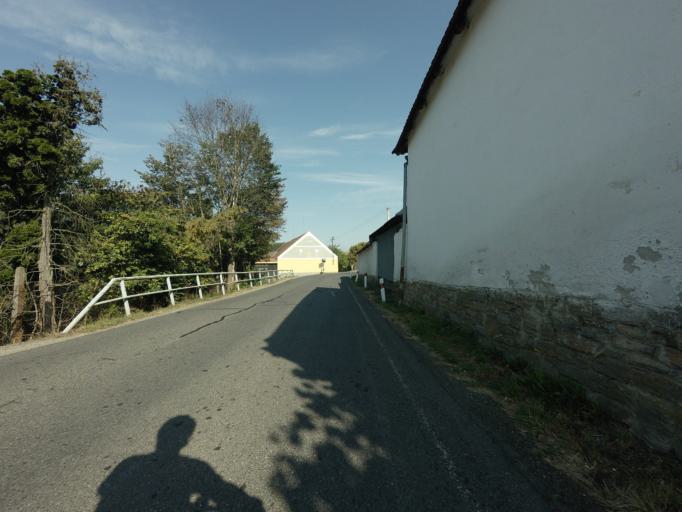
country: CZ
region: Jihocesky
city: Bernartice
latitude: 49.3264
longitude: 14.3580
